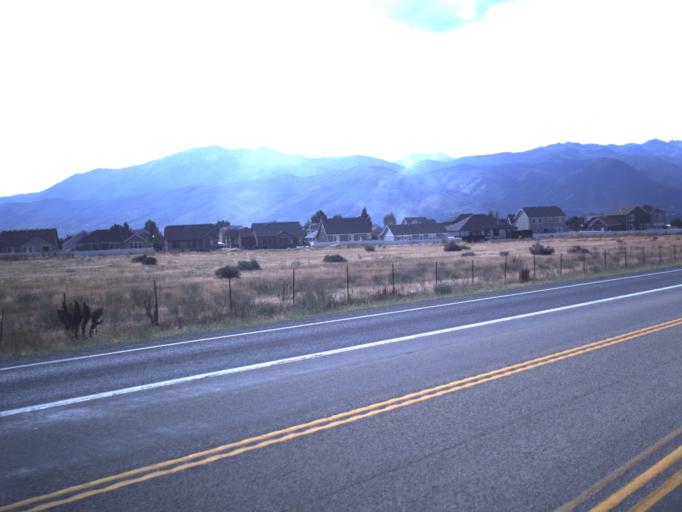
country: US
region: Utah
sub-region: Wasatch County
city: Heber
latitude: 40.4820
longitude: -111.4021
